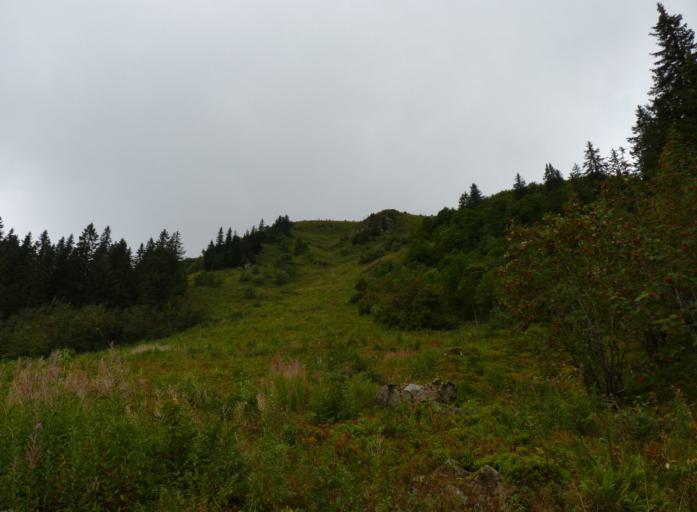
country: DE
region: Baden-Wuerttemberg
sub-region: Freiburg Region
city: Oberried
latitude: 47.8783
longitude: 8.0069
